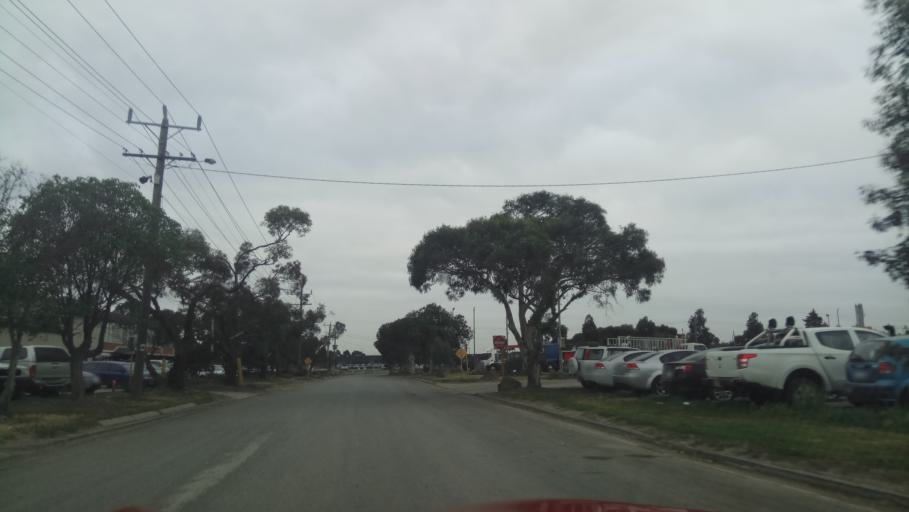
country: AU
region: Victoria
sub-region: Hobsons Bay
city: Altona North
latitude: -37.8402
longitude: 144.8197
